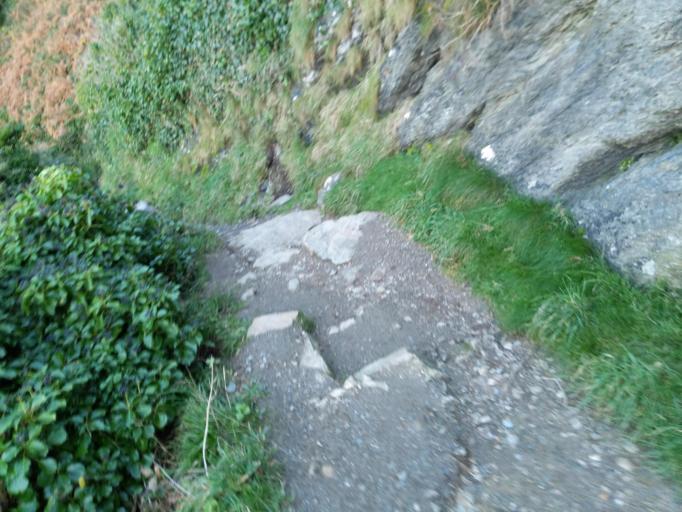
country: GB
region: England
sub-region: Cornwall
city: Fowey
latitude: 50.3285
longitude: -4.6026
